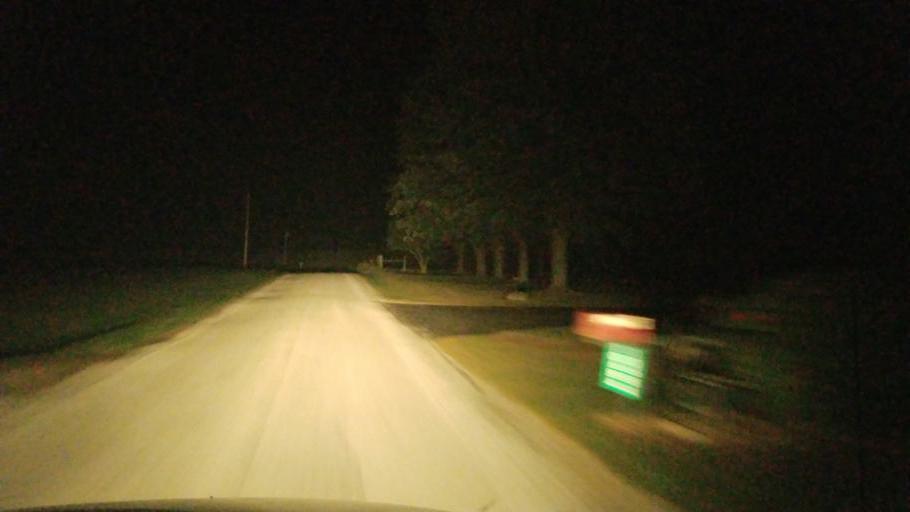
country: US
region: Ohio
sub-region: Highland County
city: Leesburg
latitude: 39.3041
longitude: -83.5627
